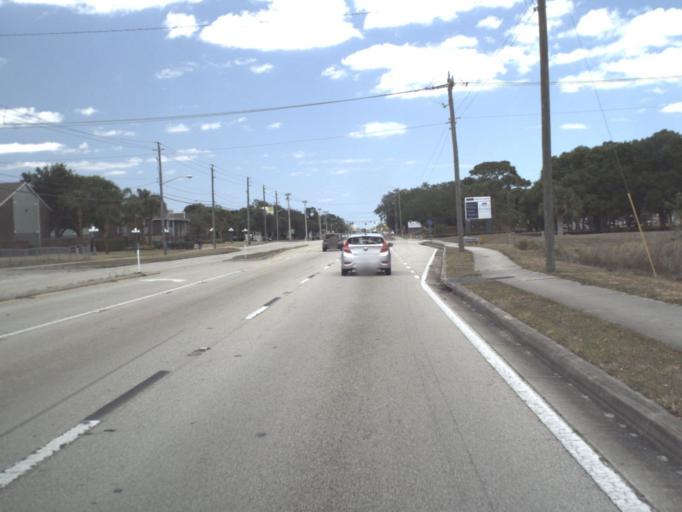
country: US
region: Florida
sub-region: Brevard County
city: Melbourne
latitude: 28.0527
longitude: -80.6214
